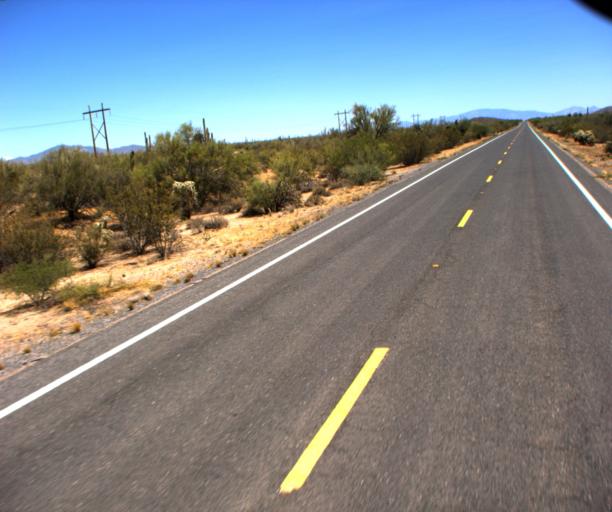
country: US
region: Arizona
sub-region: Pinal County
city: Florence
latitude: 32.8098
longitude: -111.1918
